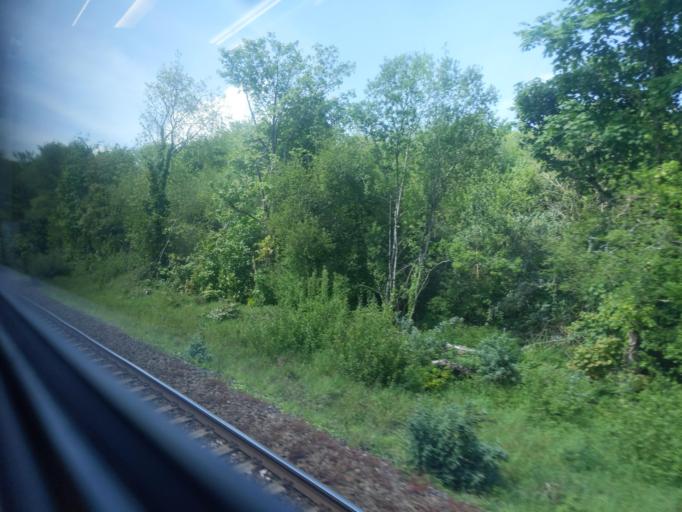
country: GB
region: England
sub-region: Cornwall
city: St Austell
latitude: 50.3436
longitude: -4.8062
